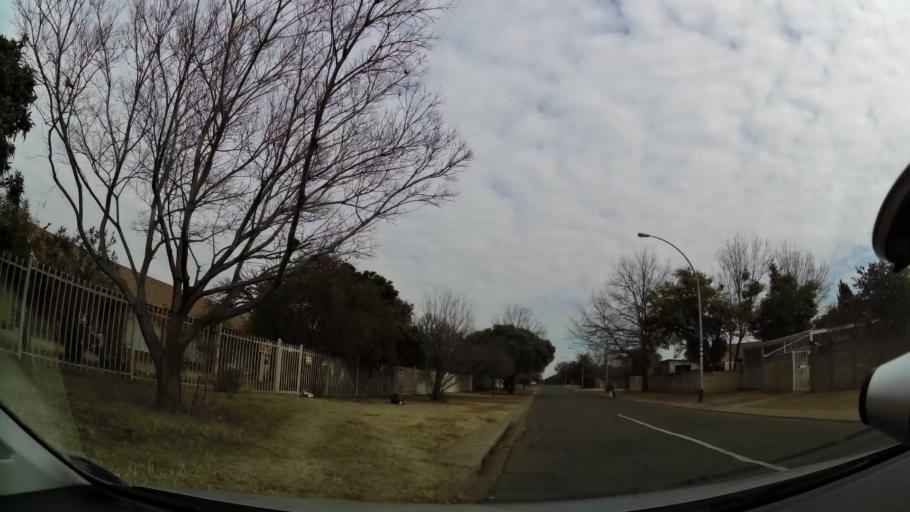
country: ZA
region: Orange Free State
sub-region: Mangaung Metropolitan Municipality
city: Bloemfontein
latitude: -29.1288
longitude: 26.1684
